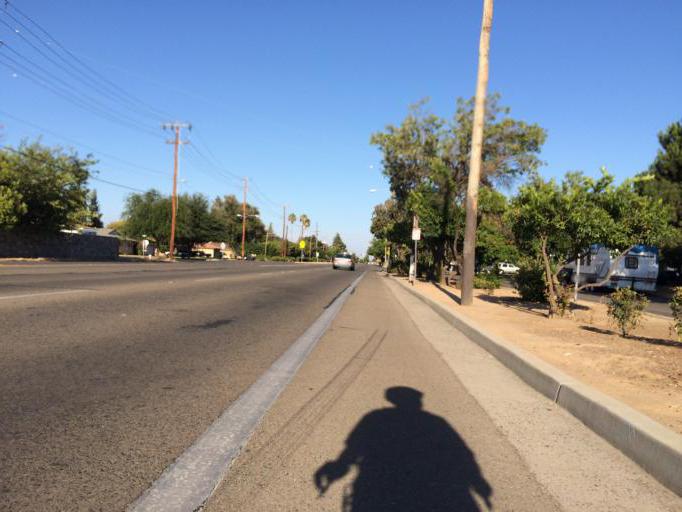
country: US
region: California
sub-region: Fresno County
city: Clovis
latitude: 36.8157
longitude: -119.7682
